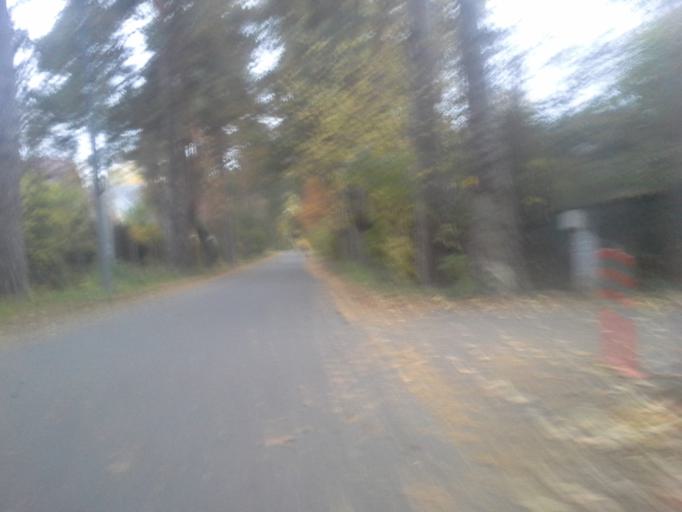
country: RU
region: Moscow
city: Tolstopal'tsevo
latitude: 55.6345
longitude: 37.2551
